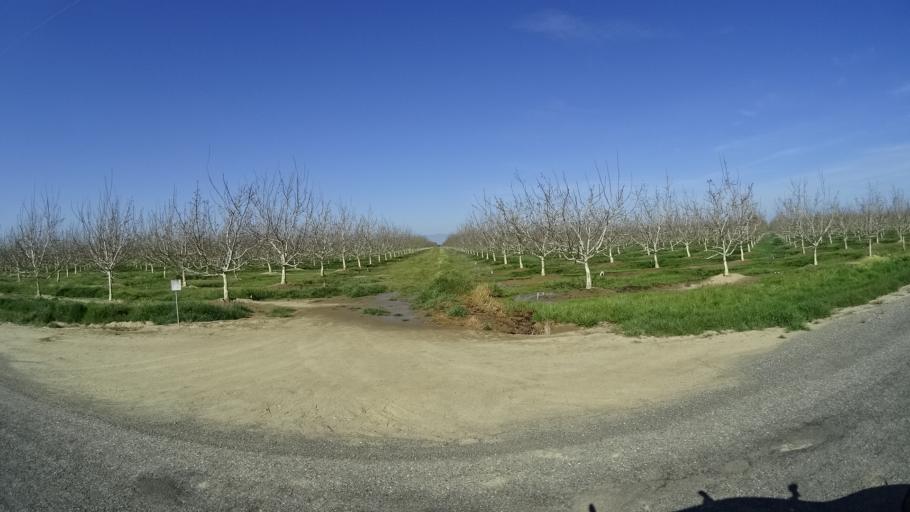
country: US
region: California
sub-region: Glenn County
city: Willows
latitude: 39.6142
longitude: -122.1170
